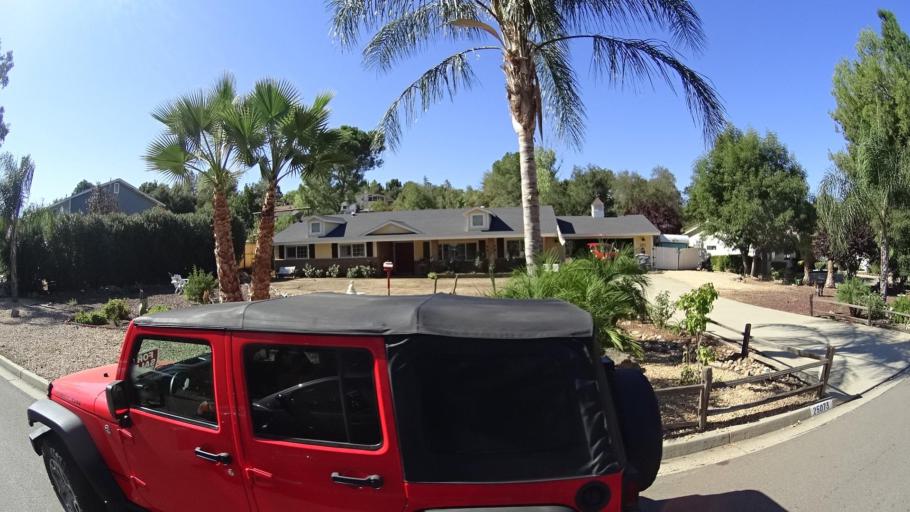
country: US
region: California
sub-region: San Diego County
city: San Diego Country Estates
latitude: 33.0048
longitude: -116.7875
